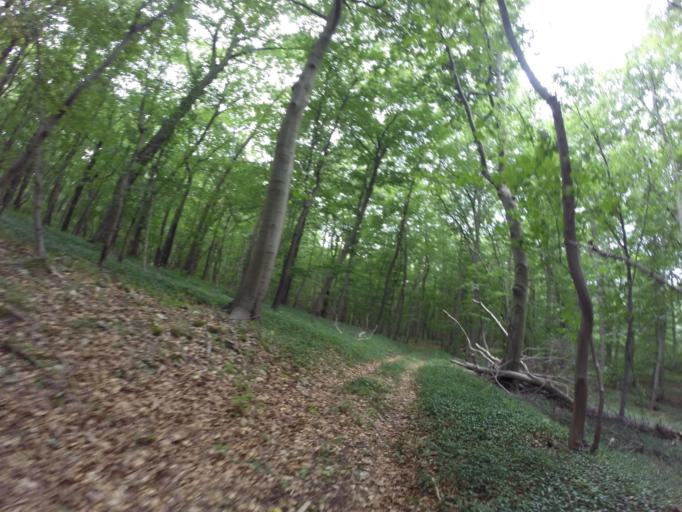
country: DE
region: Thuringia
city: Golmsdorf
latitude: 50.9600
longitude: 11.6548
